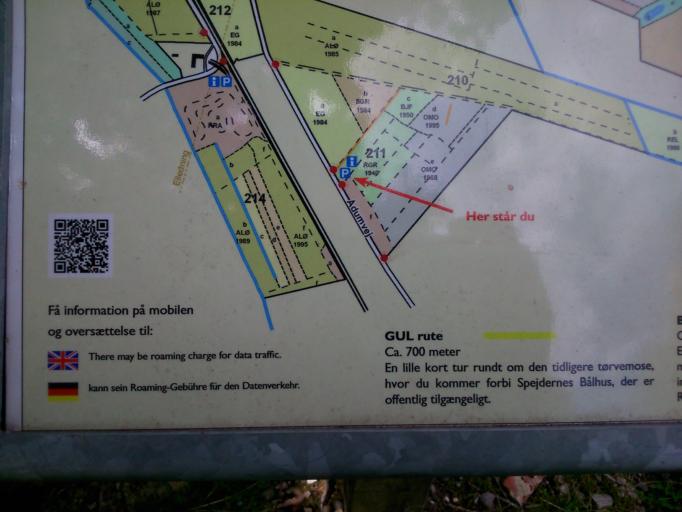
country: DK
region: Central Jutland
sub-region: Ringkobing-Skjern Kommune
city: Tarm
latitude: 55.8967
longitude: 8.5383
